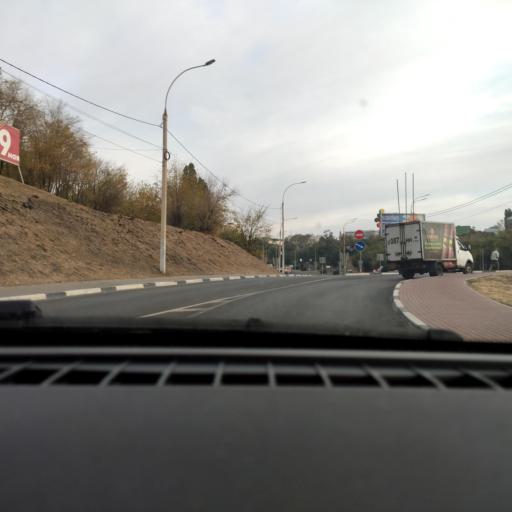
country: RU
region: Voronezj
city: Voronezh
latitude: 51.6681
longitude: 39.2202
